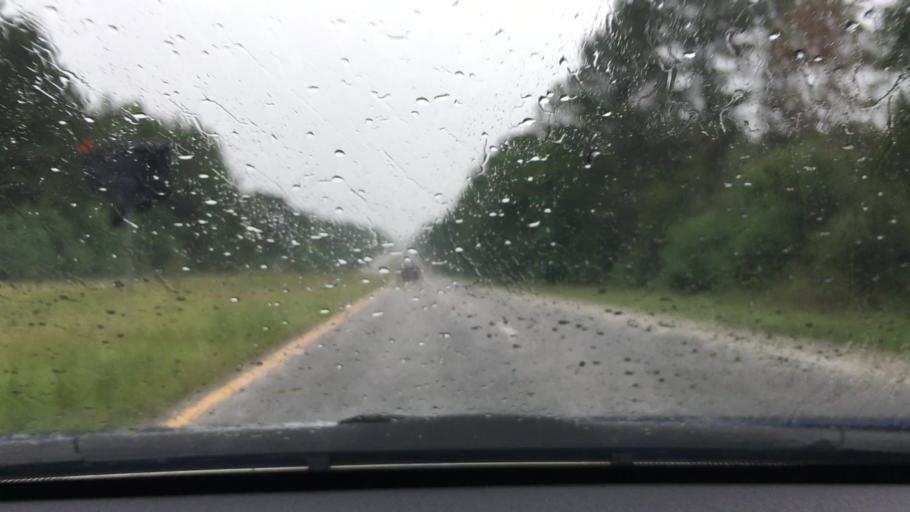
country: US
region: South Carolina
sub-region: Sumter County
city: Stateburg
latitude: 33.9499
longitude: -80.5518
